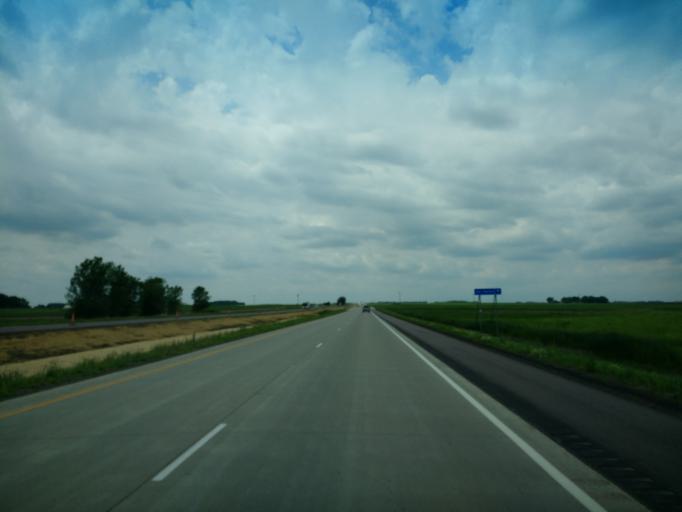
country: US
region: Minnesota
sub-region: Cottonwood County
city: Mountain Lake
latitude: 43.9255
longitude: -94.9746
